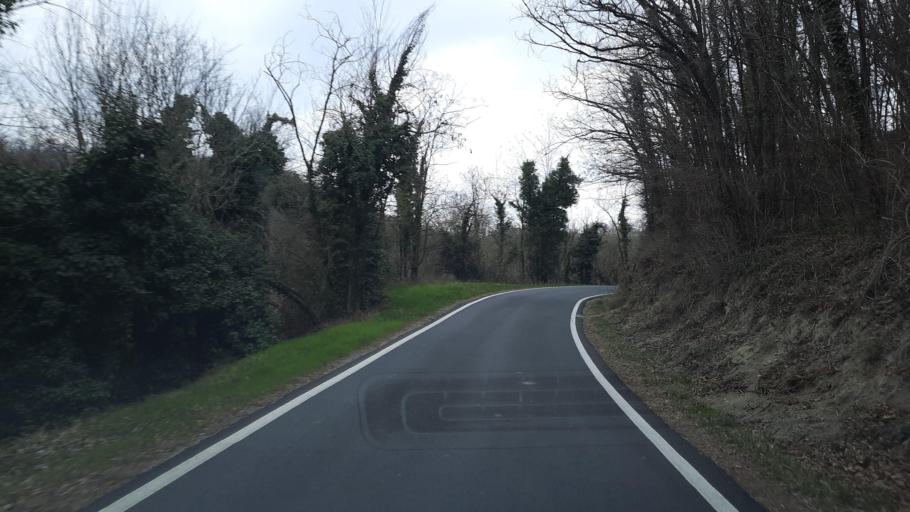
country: IT
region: Piedmont
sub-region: Provincia di Alessandria
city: Odalengo Grande
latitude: 45.1025
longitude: 8.1744
